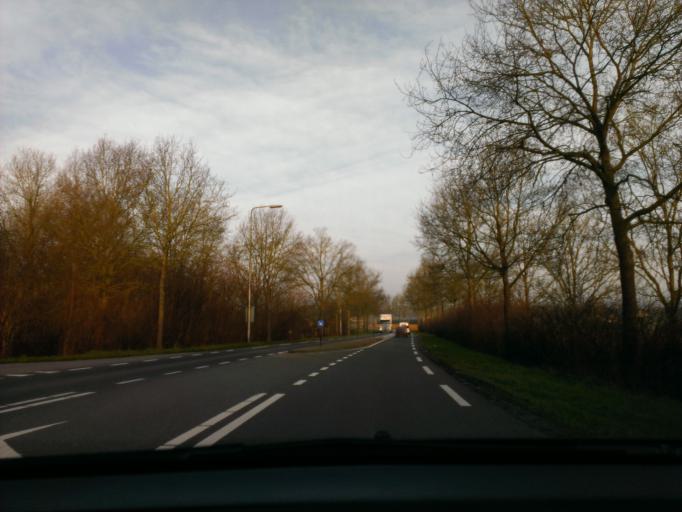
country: NL
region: Gelderland
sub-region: Gemeente Epe
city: Vaassen
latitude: 52.2916
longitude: 6.0066
